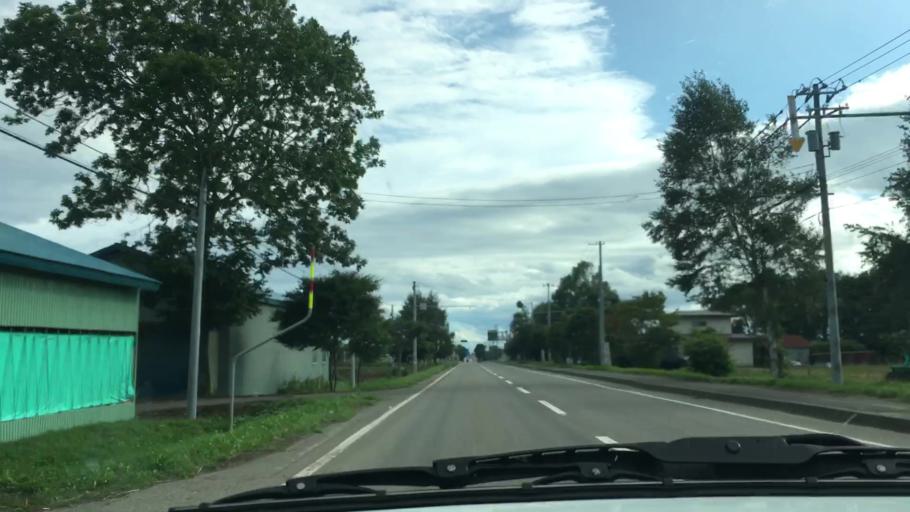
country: JP
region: Hokkaido
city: Otofuke
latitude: 43.2420
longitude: 143.2972
